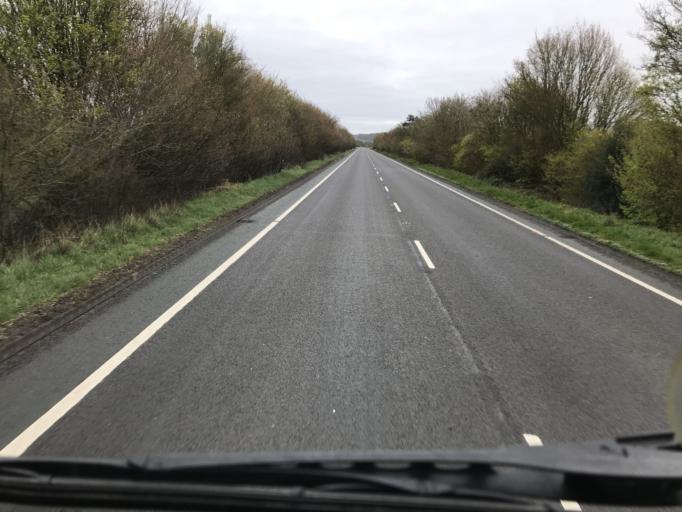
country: GB
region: England
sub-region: Cheshire West and Chester
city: Tattenhall
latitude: 53.1152
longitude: -2.7952
